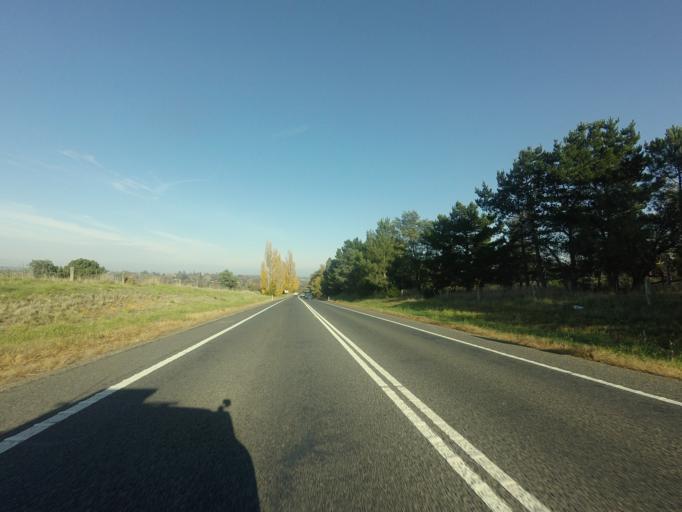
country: AU
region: Tasmania
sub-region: Northern Midlands
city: Longford
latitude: -41.5828
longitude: 147.1320
